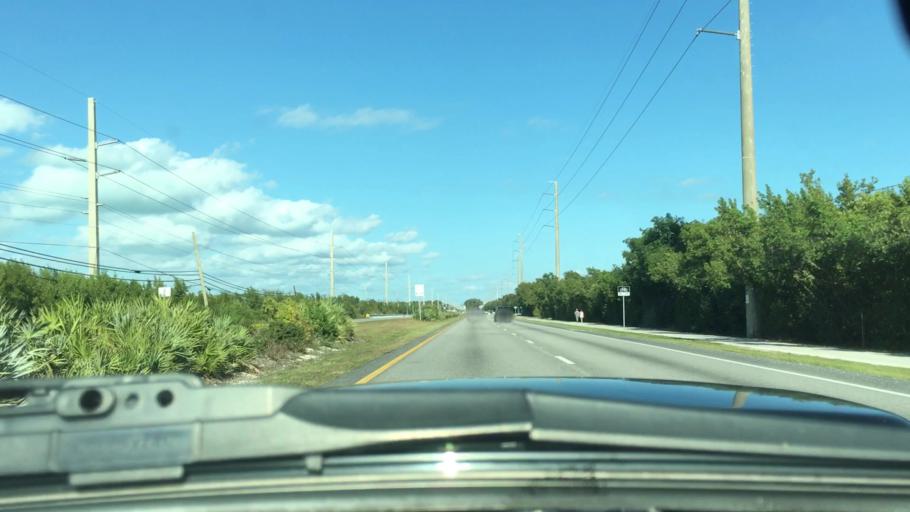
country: US
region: Florida
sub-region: Monroe County
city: Tavernier
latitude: 25.0274
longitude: -80.5069
